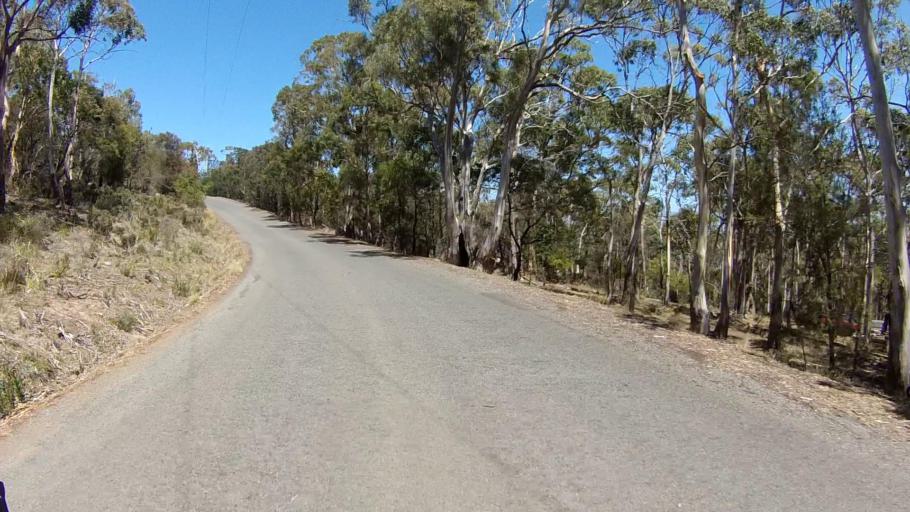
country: AU
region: Tasmania
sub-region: Clarence
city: Cambridge
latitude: -42.8454
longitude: 147.4321
